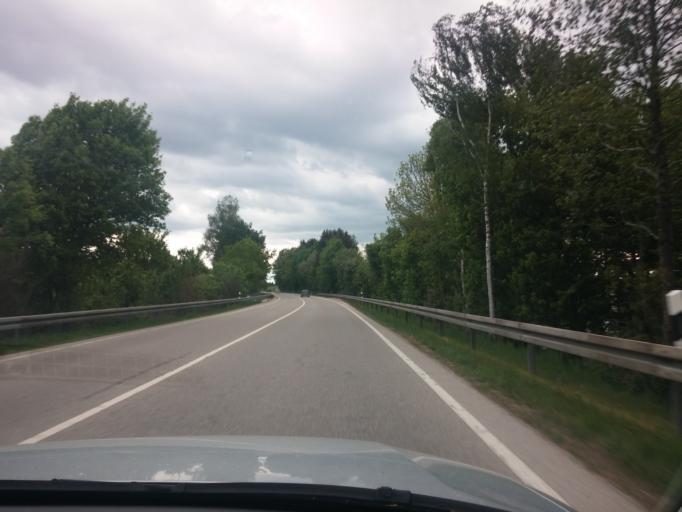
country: DE
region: Bavaria
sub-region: Upper Bavaria
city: Sachsenkam
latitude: 47.8067
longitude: 11.6513
